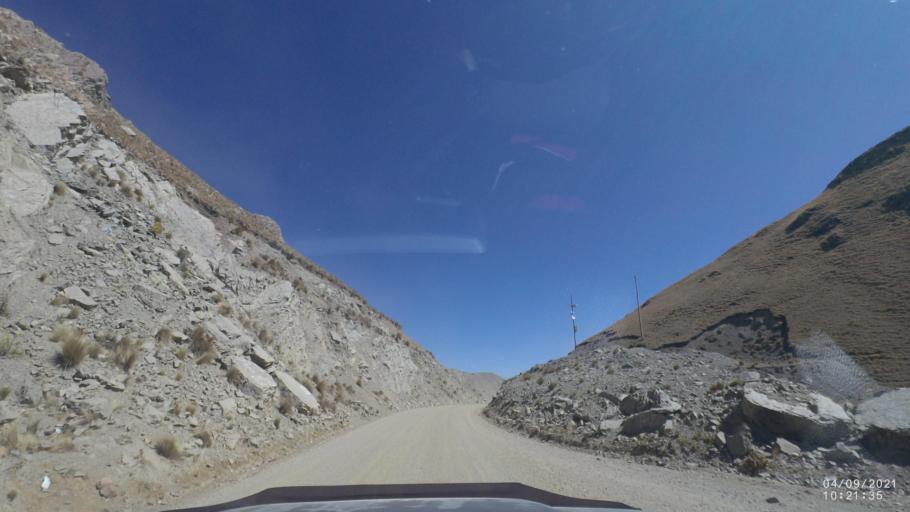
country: BO
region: Cochabamba
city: Sipe Sipe
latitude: -17.3102
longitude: -66.4325
